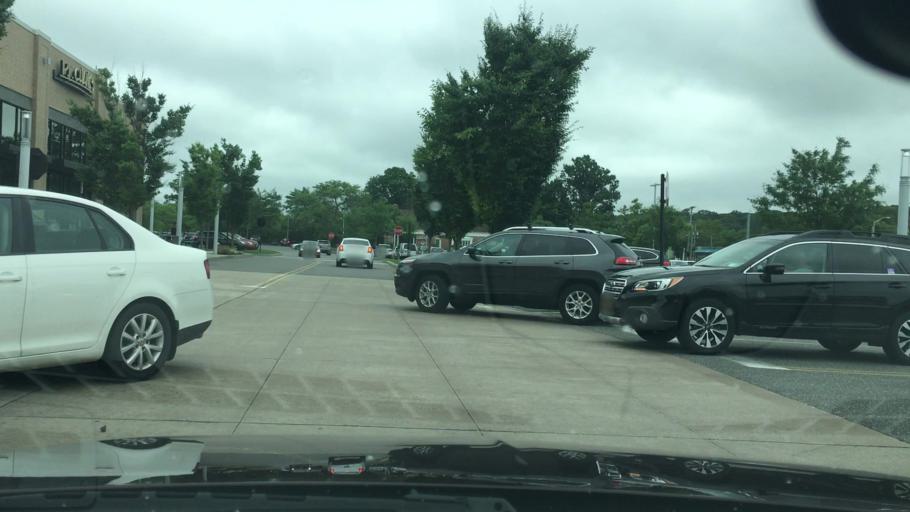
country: US
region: New York
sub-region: Suffolk County
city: South Huntington
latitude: 40.8211
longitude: -73.4110
